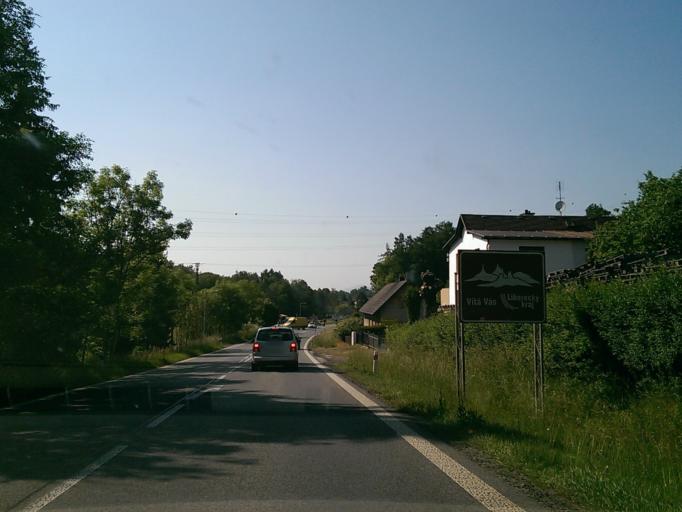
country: CZ
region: Liberecky
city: Rovensko pod Troskami
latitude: 50.5154
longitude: 15.2529
